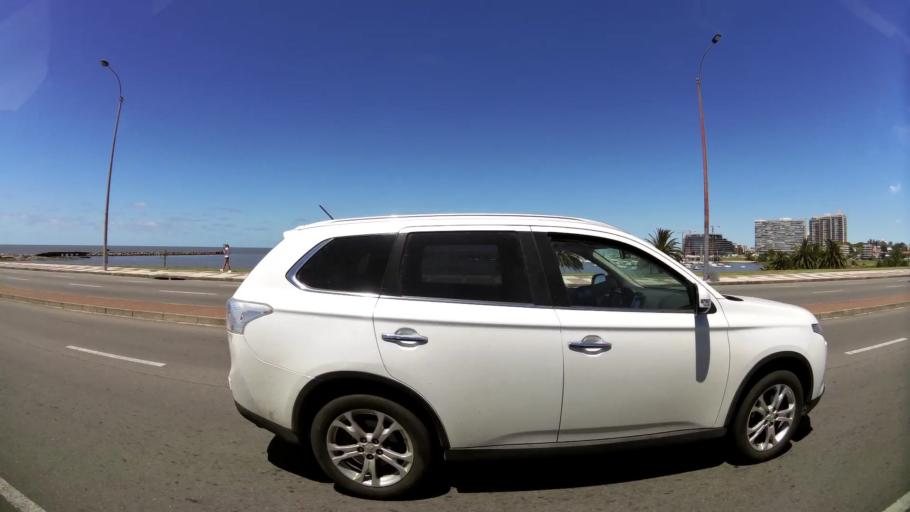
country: UY
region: Montevideo
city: Montevideo
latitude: -34.9052
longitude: -56.1279
